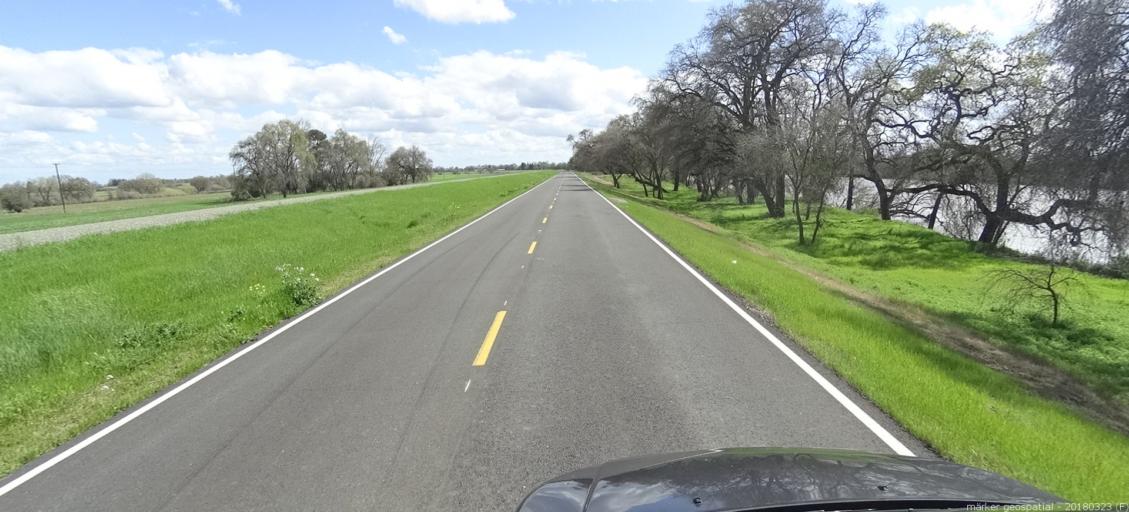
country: US
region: California
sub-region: Yolo County
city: West Sacramento
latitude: 38.6560
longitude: -121.6026
